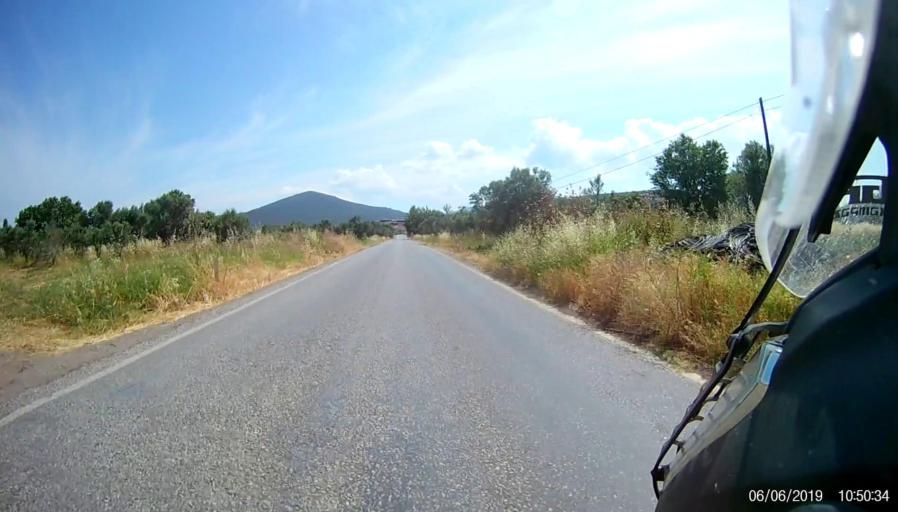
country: TR
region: Canakkale
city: Ayvacik
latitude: 39.5198
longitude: 26.4505
